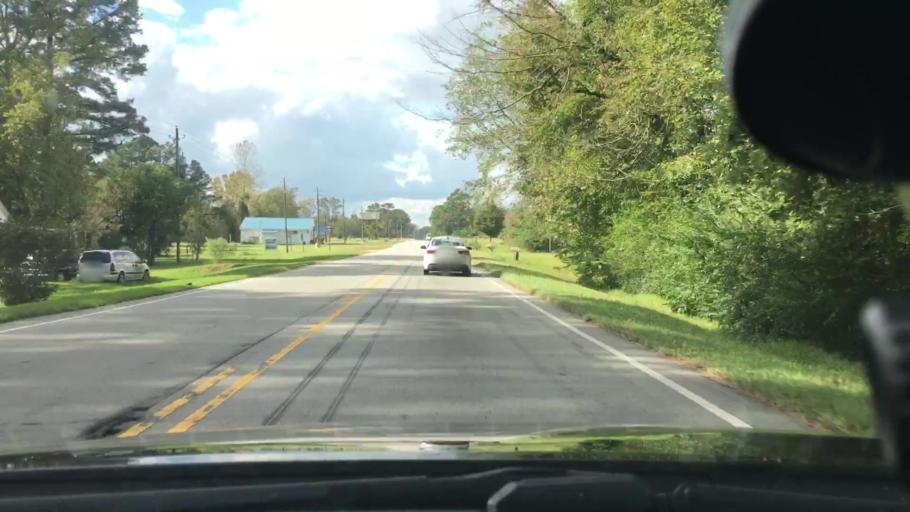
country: US
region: North Carolina
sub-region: Craven County
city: Vanceboro
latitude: 35.2692
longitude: -77.1102
